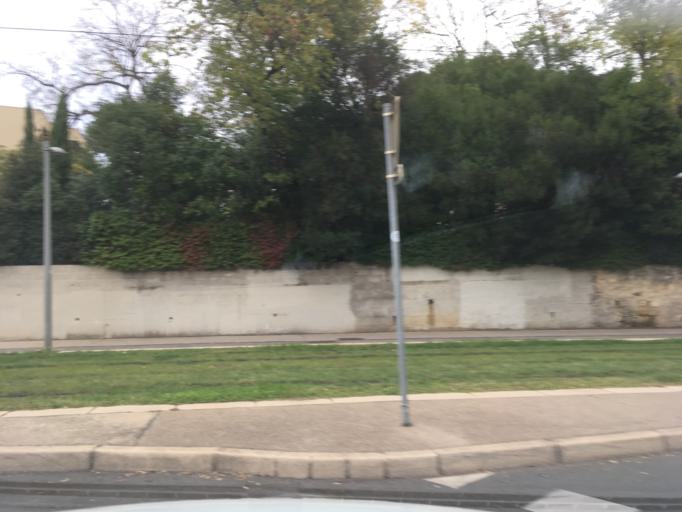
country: FR
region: Languedoc-Roussillon
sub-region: Departement de l'Herault
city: Montpellier
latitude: 43.6219
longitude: 3.8830
